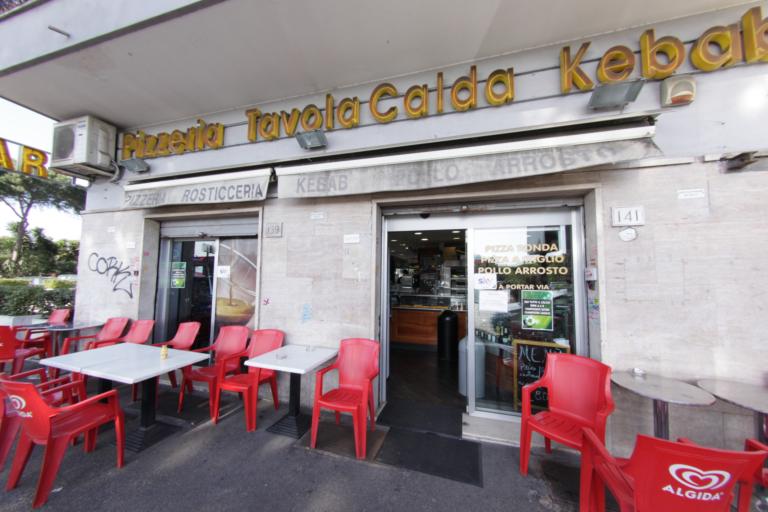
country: IT
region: Latium
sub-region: Citta metropolitana di Roma Capitale
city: Rome
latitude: 41.8448
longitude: 12.4801
